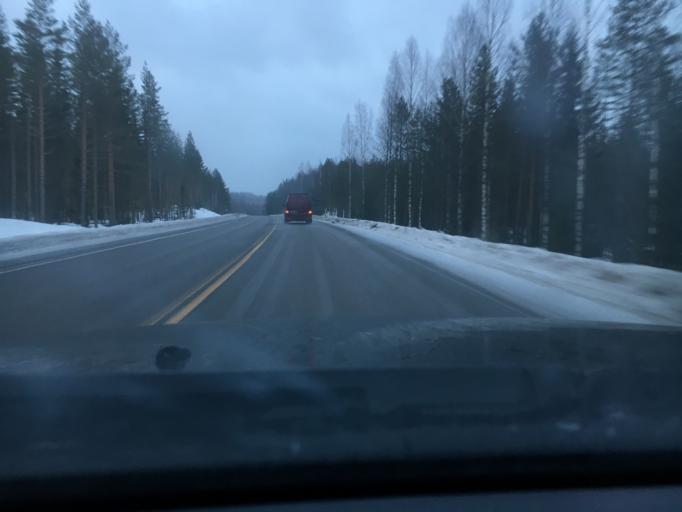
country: FI
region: Central Finland
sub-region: Jyvaeskylae
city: Hankasalmi
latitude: 62.4102
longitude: 26.6869
